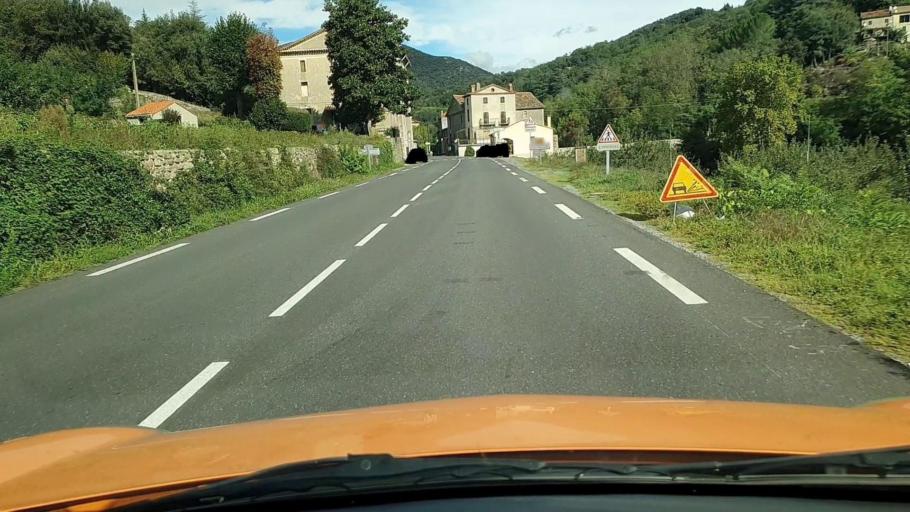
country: FR
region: Languedoc-Roussillon
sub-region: Departement du Gard
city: Valleraugue
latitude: 44.0316
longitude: 3.6786
